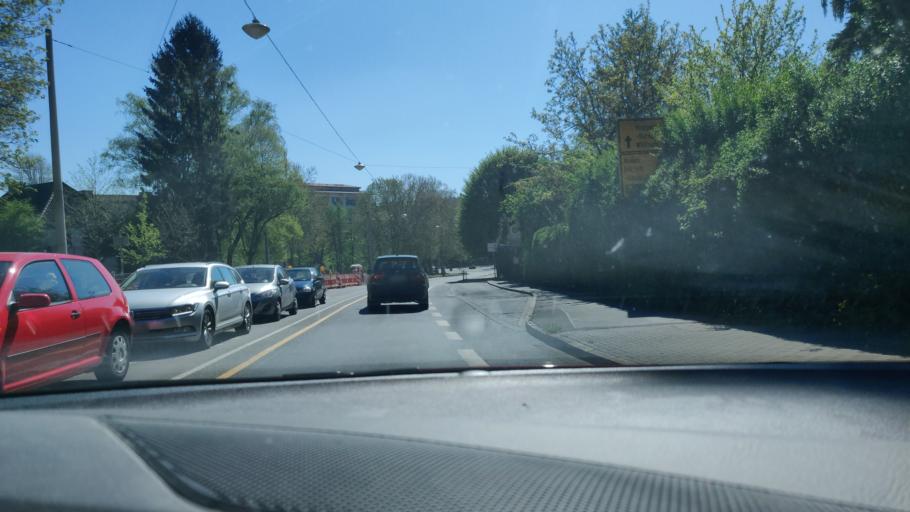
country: DE
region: North Rhine-Westphalia
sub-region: Regierungsbezirk Dusseldorf
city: Mettmann
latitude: 51.2494
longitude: 6.9721
